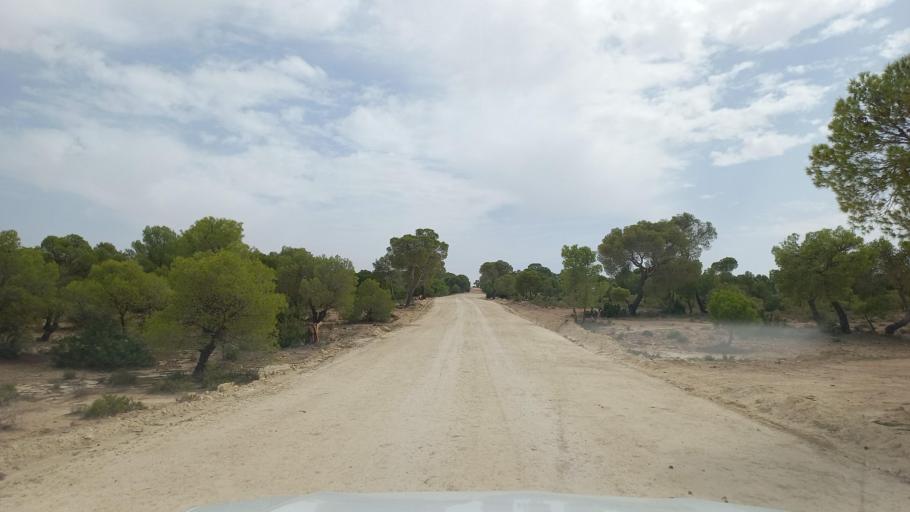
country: TN
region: Al Qasrayn
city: Kasserine
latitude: 35.3808
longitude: 8.8685
